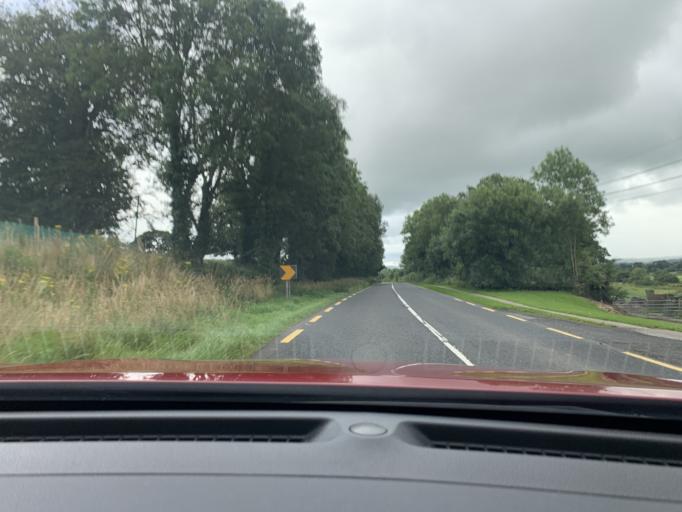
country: IE
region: Ulster
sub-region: County Donegal
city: Raphoe
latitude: 54.8029
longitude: -7.6106
